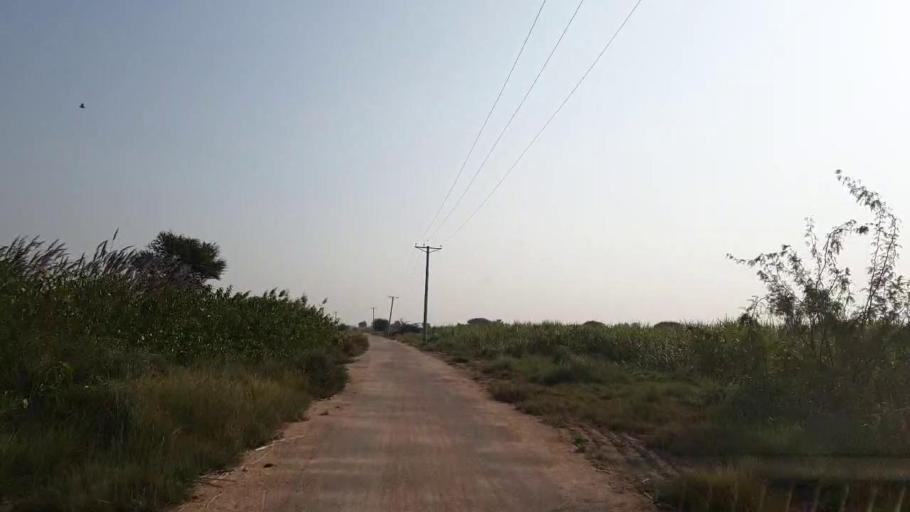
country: PK
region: Sindh
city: Bulri
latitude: 24.9775
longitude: 68.3781
